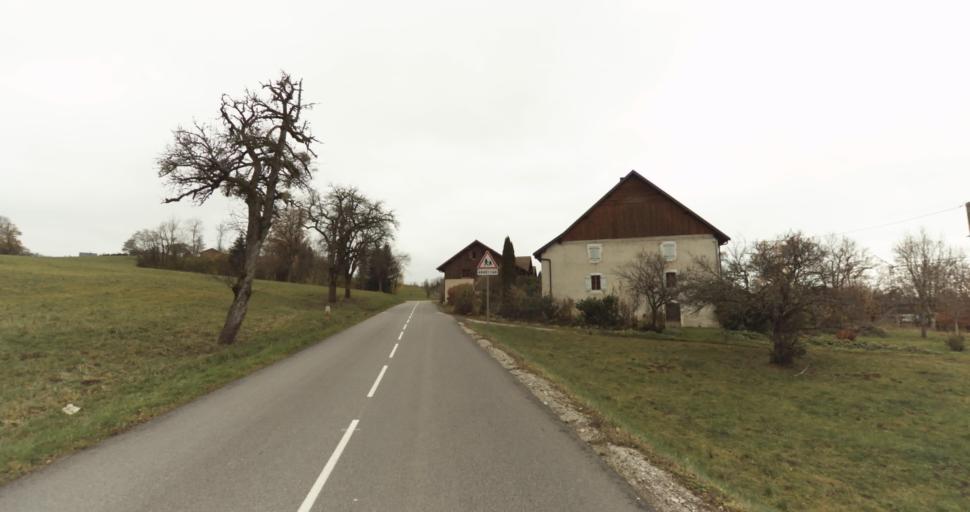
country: FR
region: Rhone-Alpes
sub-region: Departement de la Haute-Savoie
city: Thorens-Glieres
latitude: 45.9869
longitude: 6.2334
